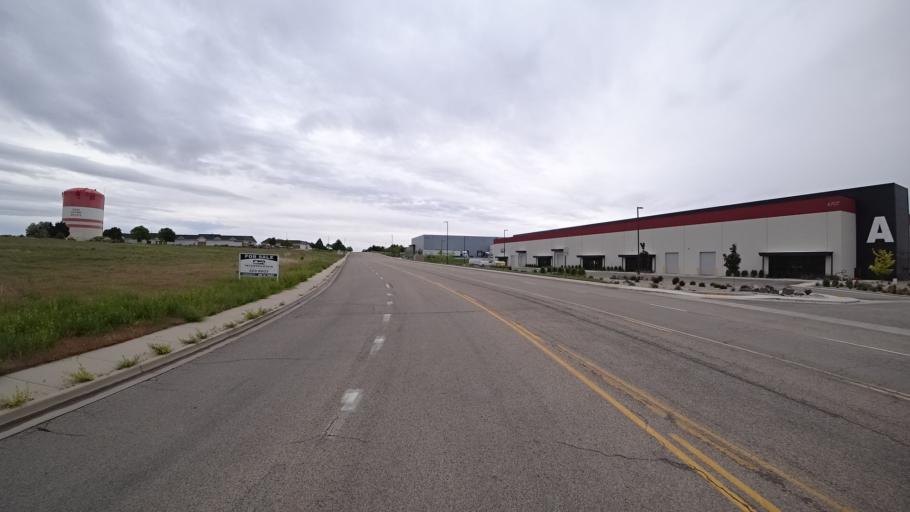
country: US
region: Idaho
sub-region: Ada County
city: Boise
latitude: 43.5418
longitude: -116.1651
